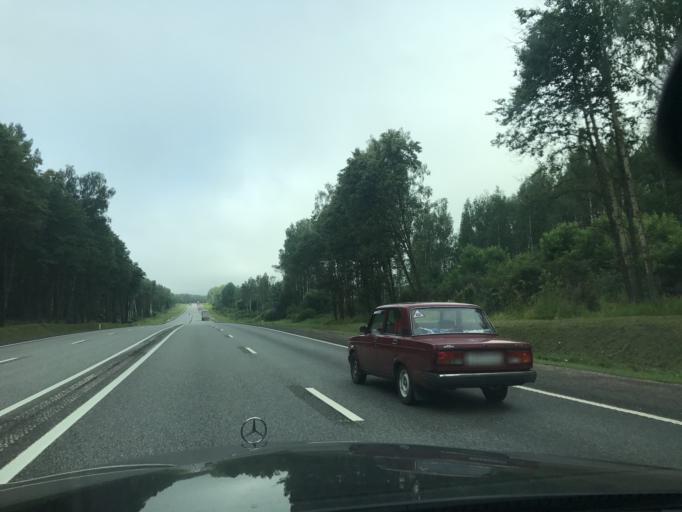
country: RU
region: Smolensk
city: Vyaz'ma
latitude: 55.3316
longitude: 34.5800
